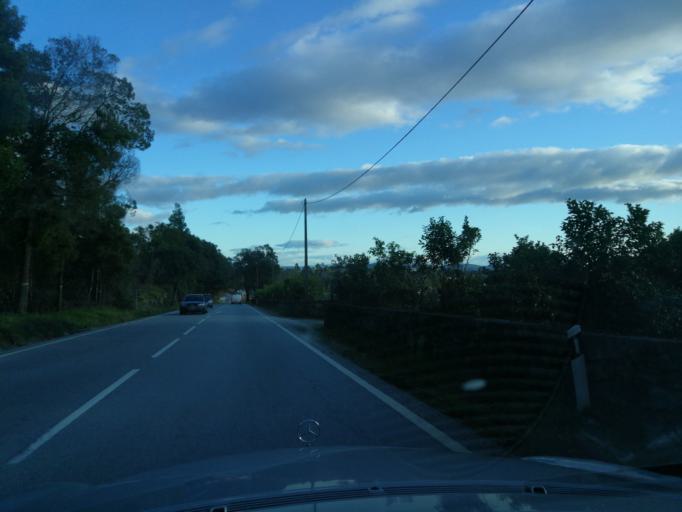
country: PT
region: Braga
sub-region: Barcelos
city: Vila Frescainha
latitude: 41.5657
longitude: -8.6647
